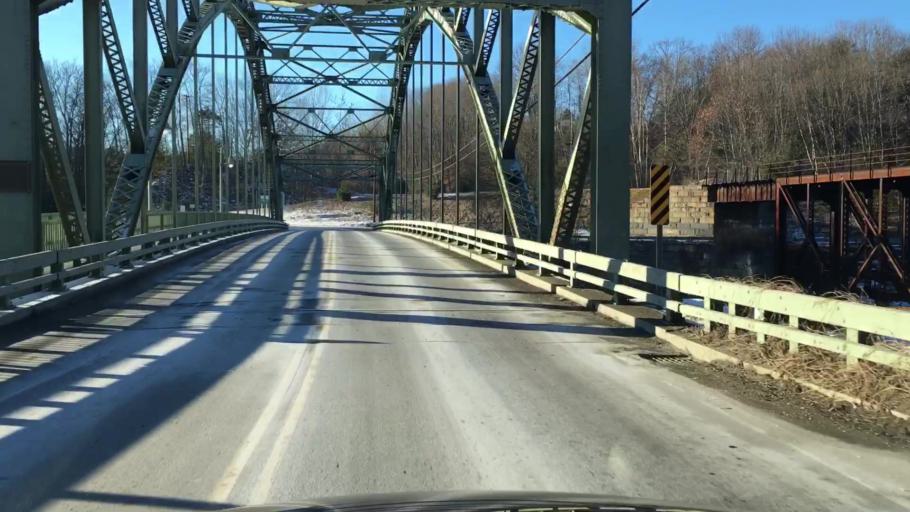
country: US
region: New Hampshire
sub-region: Grafton County
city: Woodsville
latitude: 44.1539
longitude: -72.0403
